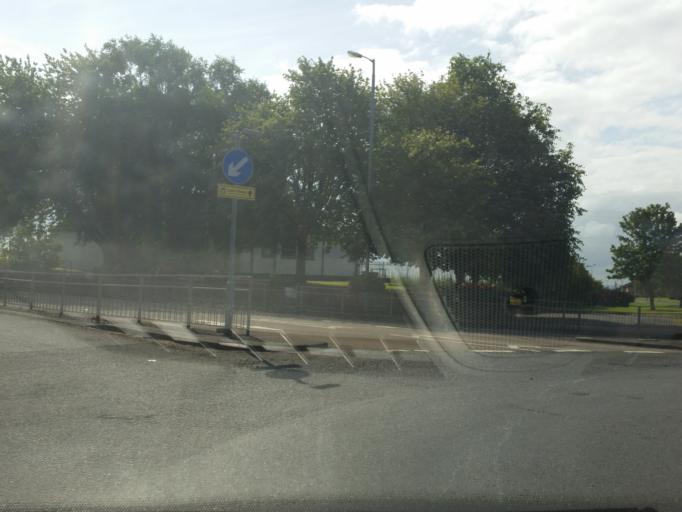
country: GB
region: Scotland
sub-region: South Lanarkshire
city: Uddingston
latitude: 55.8567
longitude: -4.0780
